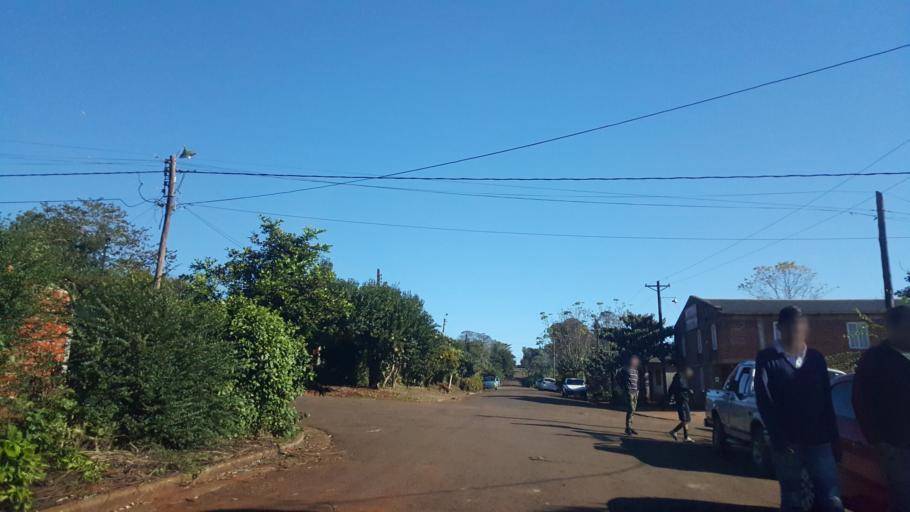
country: AR
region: Misiones
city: Gobernador Roca
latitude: -27.1871
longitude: -55.4669
